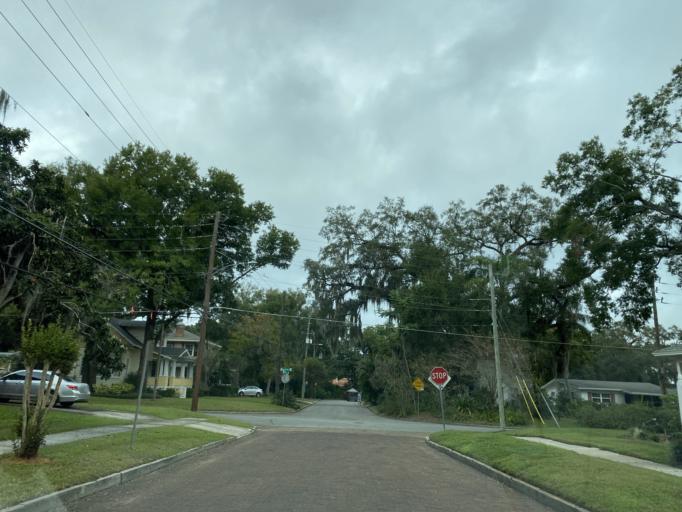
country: US
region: Florida
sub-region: Orange County
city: Orlando
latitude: 28.5543
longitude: -81.3888
